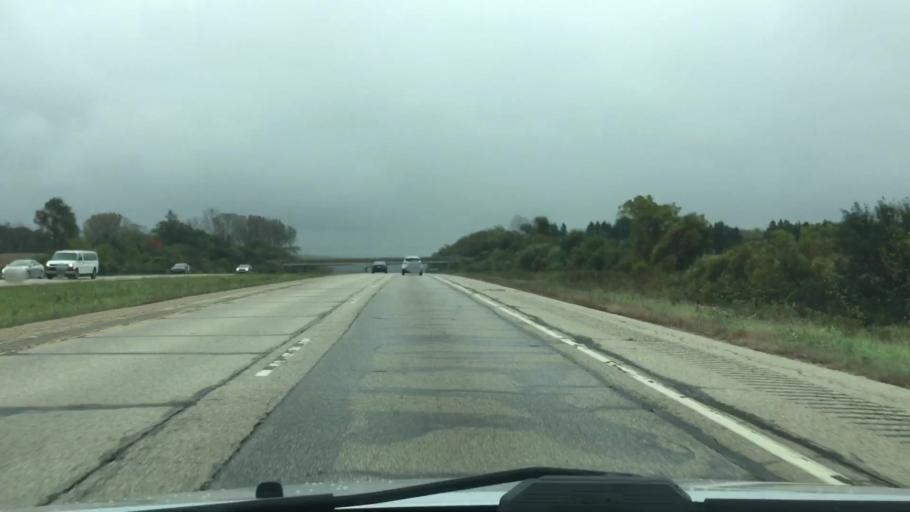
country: US
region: Wisconsin
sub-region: Walworth County
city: Como
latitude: 42.6311
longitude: -88.4733
